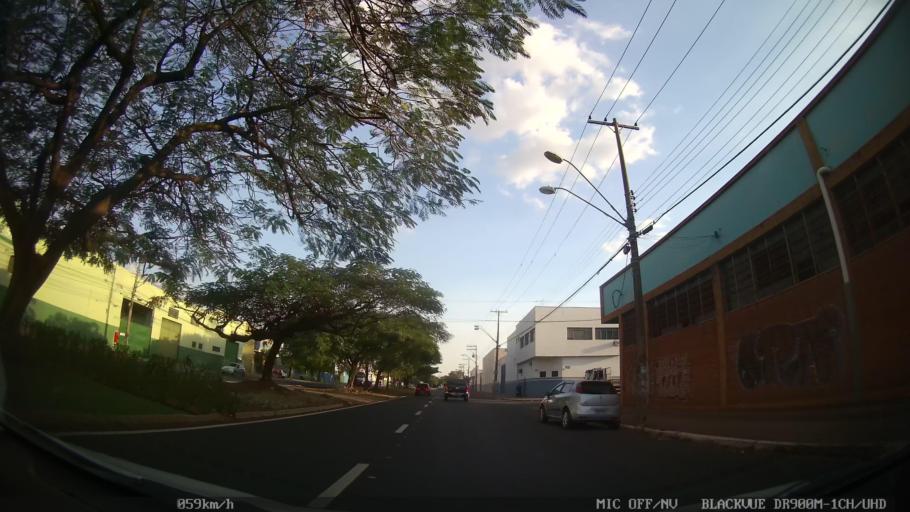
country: BR
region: Sao Paulo
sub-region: Ribeirao Preto
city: Ribeirao Preto
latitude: -21.1349
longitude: -47.7962
